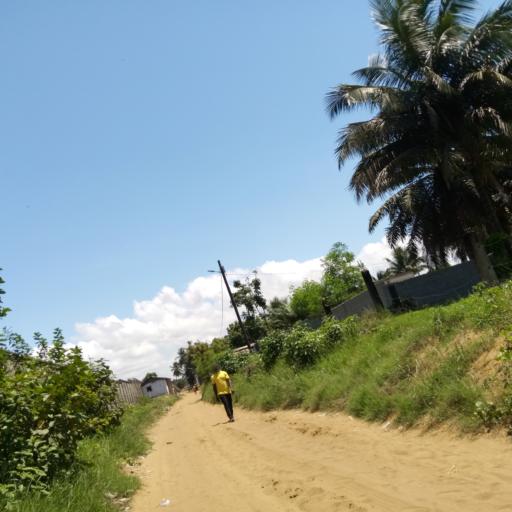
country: LR
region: Montserrado
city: Monrovia
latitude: 6.2381
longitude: -10.6952
